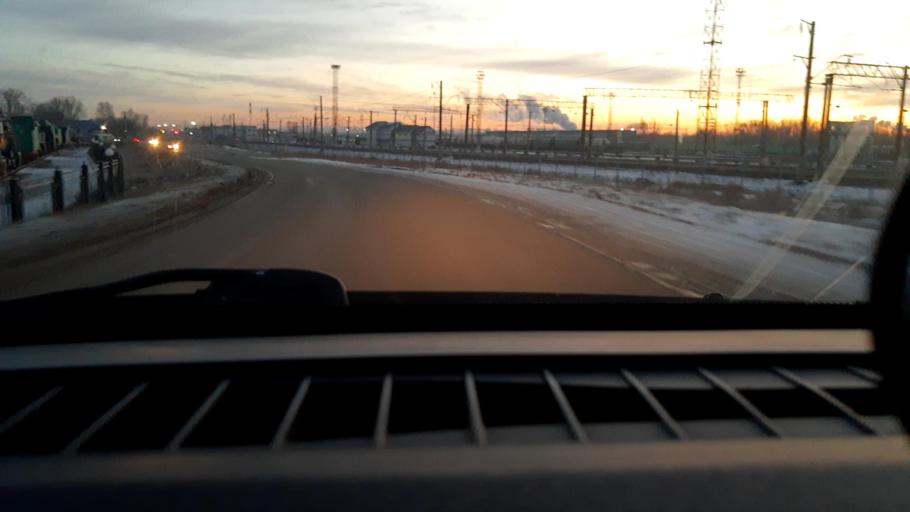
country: RU
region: Nizjnij Novgorod
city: Gorbatovka
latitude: 56.2828
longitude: 43.8433
